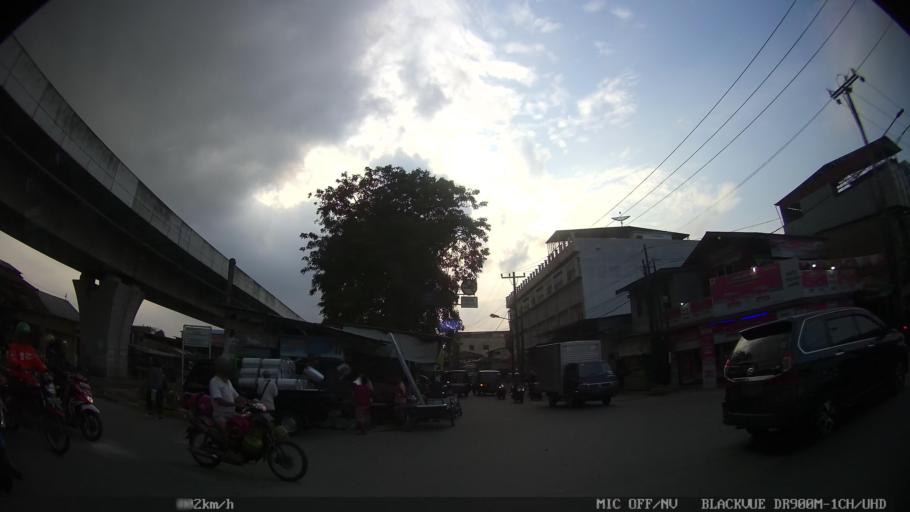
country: ID
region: North Sumatra
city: Medan
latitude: 3.5894
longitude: 98.7115
